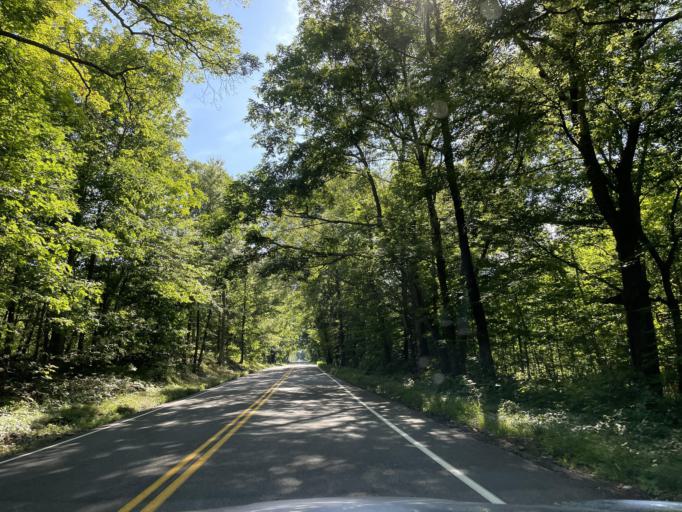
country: US
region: Massachusetts
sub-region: Worcester County
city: Sutton
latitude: 42.1435
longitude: -71.7350
